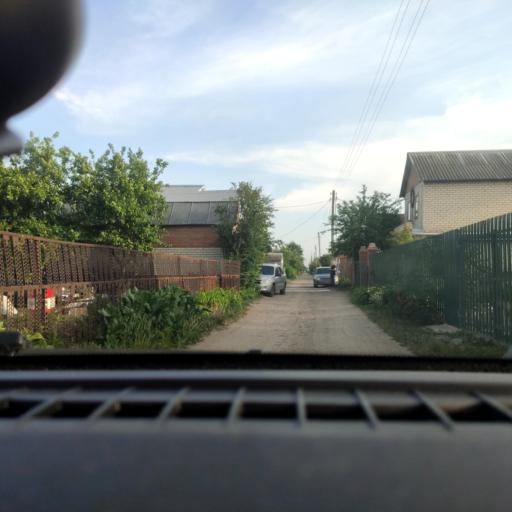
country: RU
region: Samara
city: Tol'yatti
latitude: 53.5931
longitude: 49.3238
